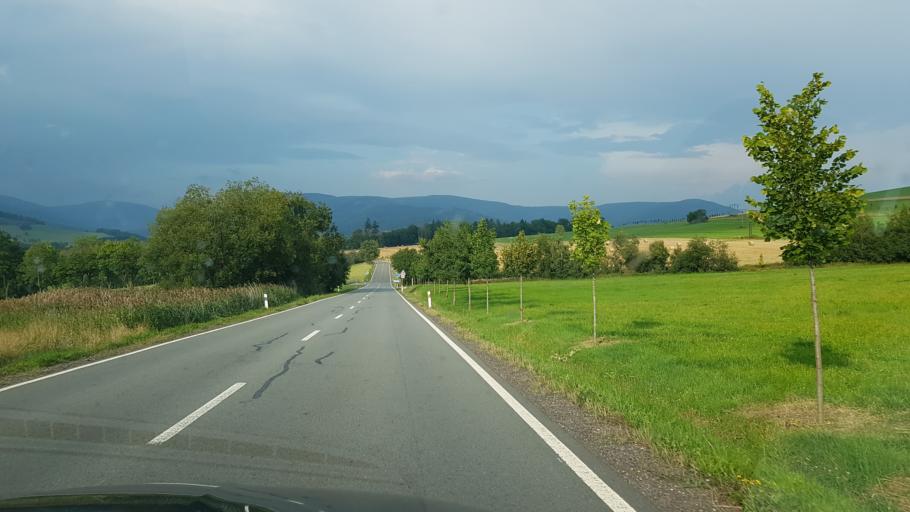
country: CZ
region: Pardubicky
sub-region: Okres Usti nad Orlici
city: Kraliky
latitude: 50.0953
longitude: 16.7741
